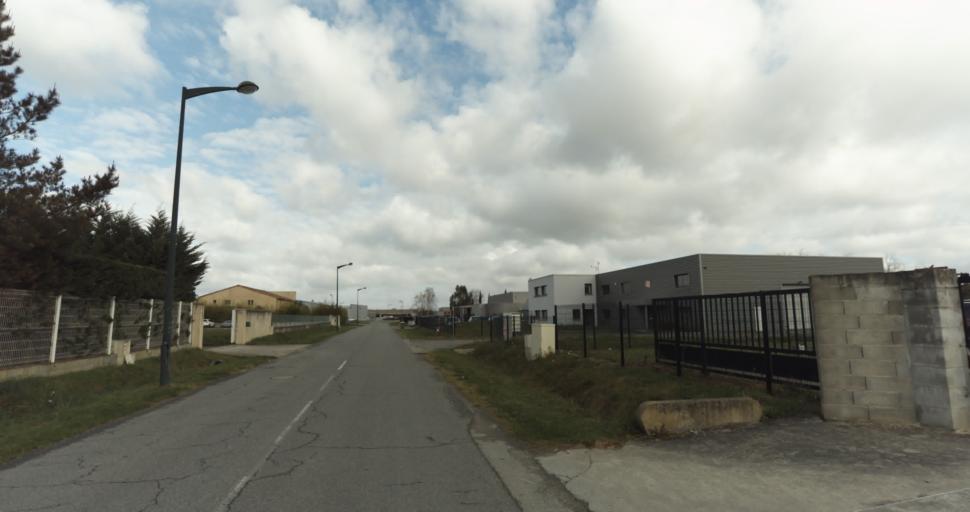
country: FR
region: Midi-Pyrenees
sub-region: Departement de la Haute-Garonne
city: Miremont
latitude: 43.3650
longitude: 1.4475
